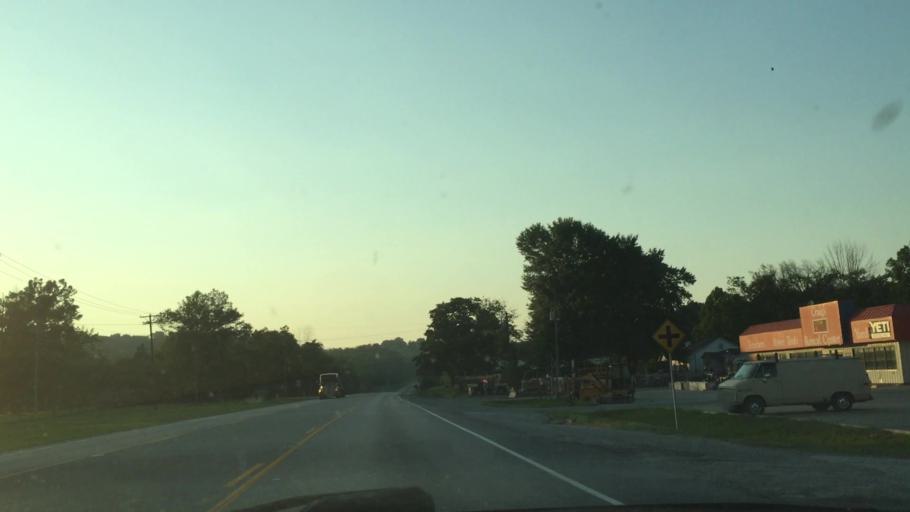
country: US
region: Kentucky
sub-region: Carroll County
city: Carrollton
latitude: 38.6664
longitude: -85.1426
